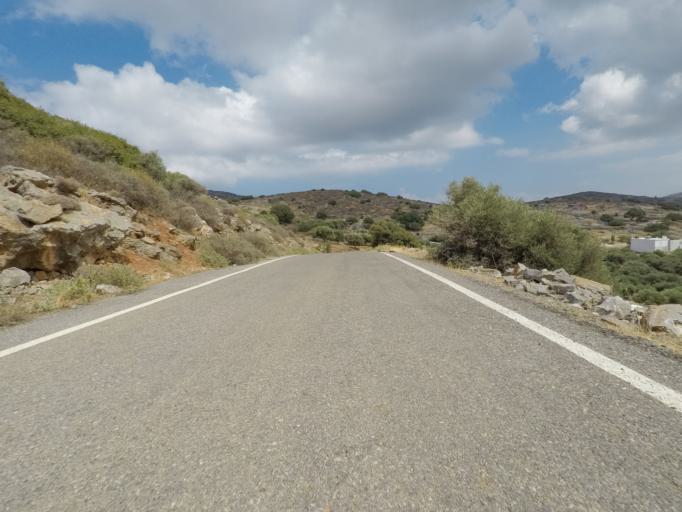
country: GR
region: Crete
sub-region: Nomos Lasithiou
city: Elounda
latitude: 35.2969
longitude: 25.6758
